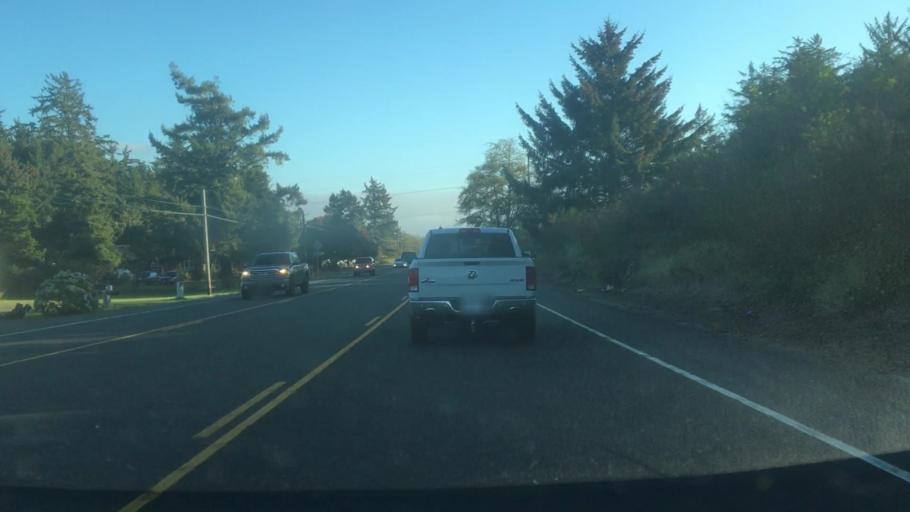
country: US
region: Oregon
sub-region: Clatsop County
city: Warrenton
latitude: 46.0990
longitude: -123.9179
